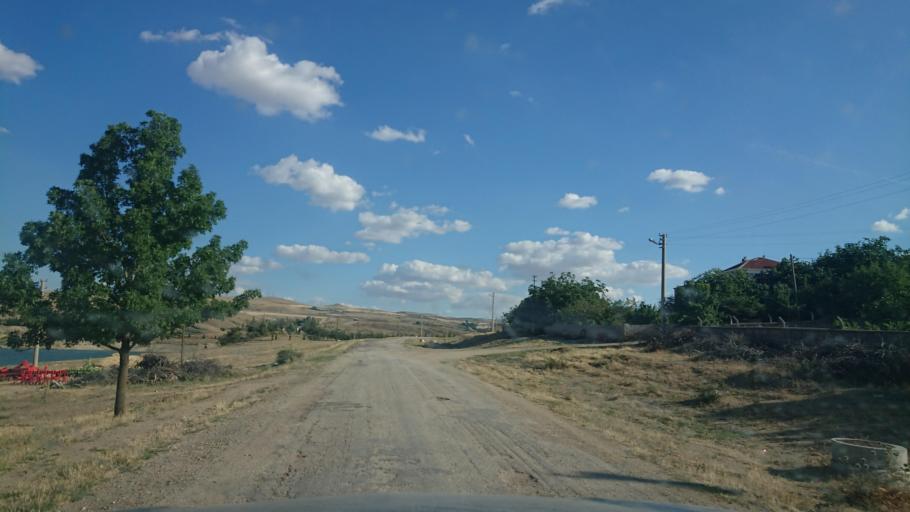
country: TR
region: Aksaray
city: Sariyahsi
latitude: 38.9550
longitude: 33.8830
